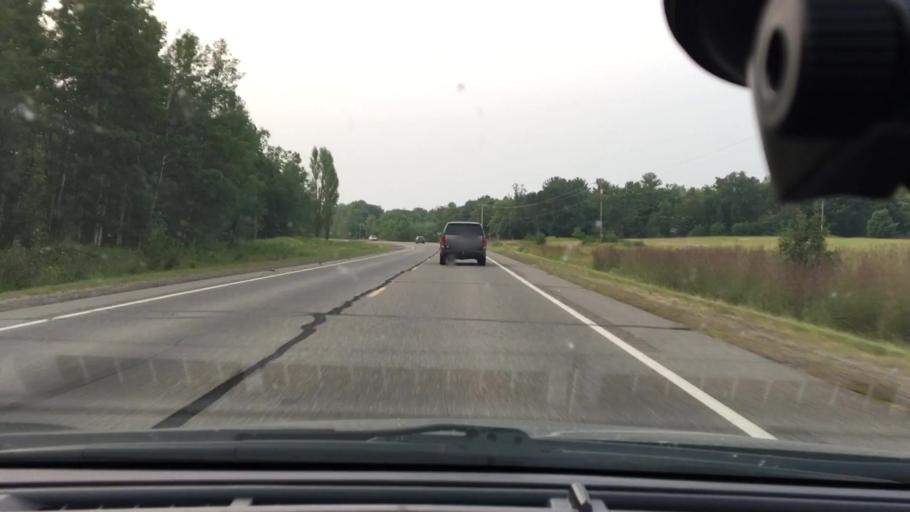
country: US
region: Minnesota
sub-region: Crow Wing County
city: Crosby
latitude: 46.4660
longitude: -93.8866
